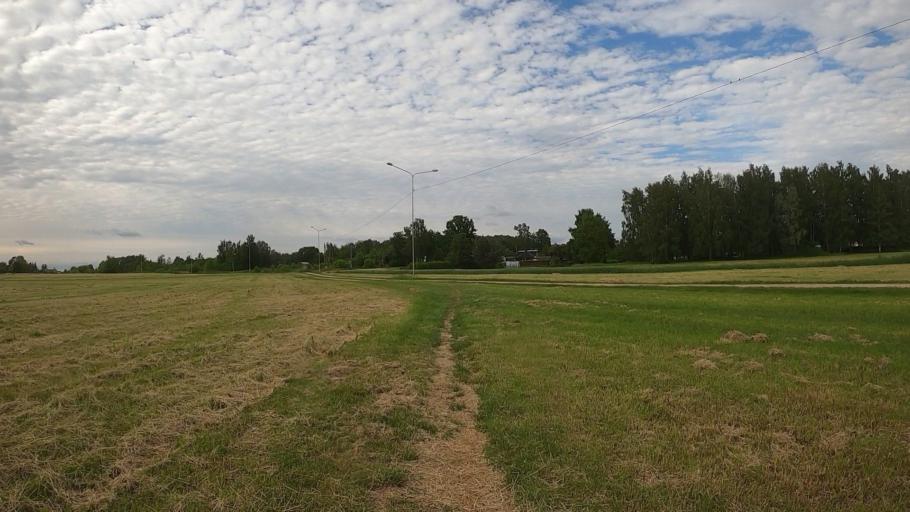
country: LV
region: Jelgava
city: Jelgava
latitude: 56.6571
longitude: 23.7376
